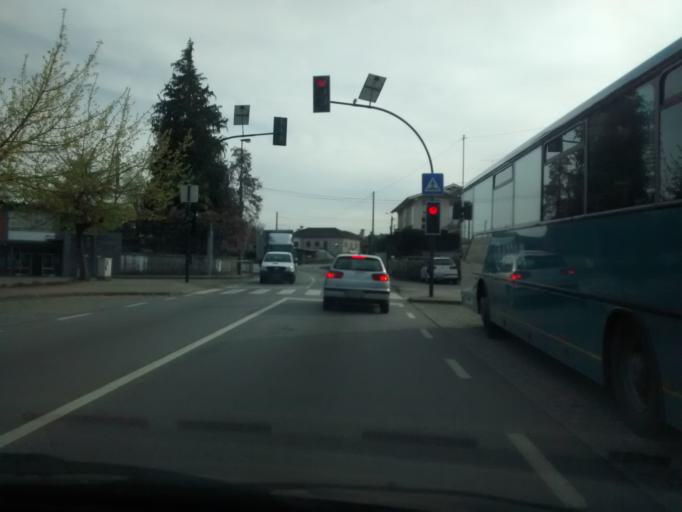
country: PT
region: Braga
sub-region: Guimaraes
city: Ponte
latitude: 41.4854
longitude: -8.3532
